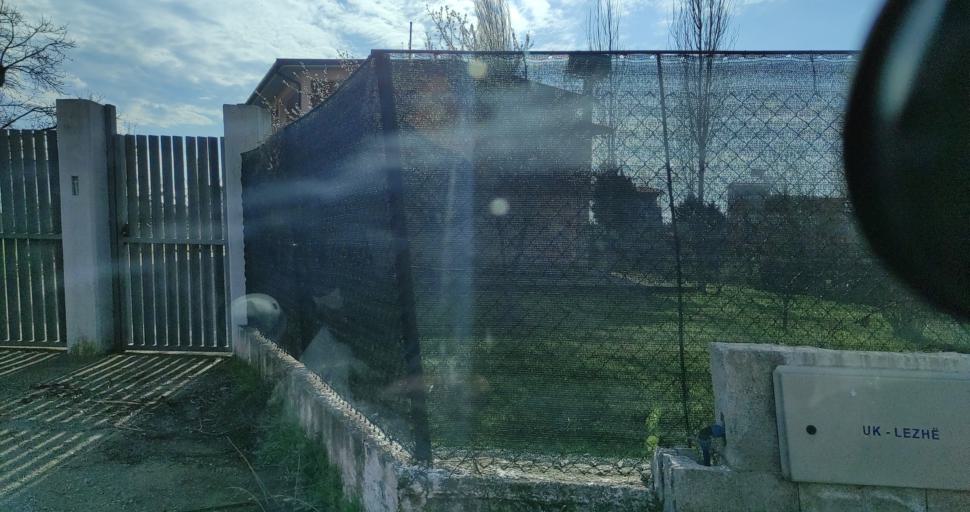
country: AL
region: Lezhe
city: Lezhe
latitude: 41.7834
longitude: 19.6297
